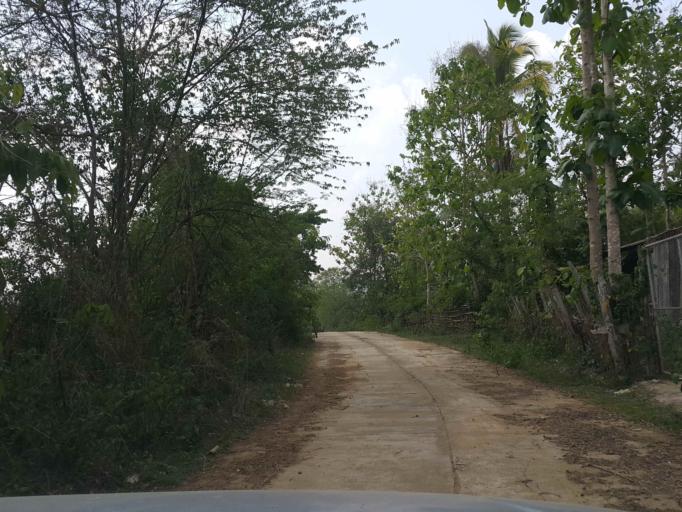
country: TH
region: Chiang Mai
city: Wiang Haeng
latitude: 19.3853
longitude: 98.7233
